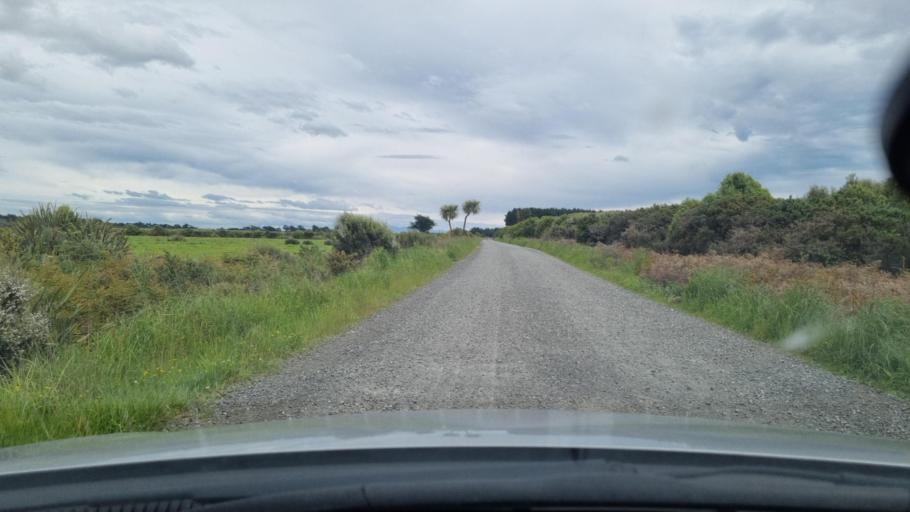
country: NZ
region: Southland
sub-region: Invercargill City
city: Invercargill
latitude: -46.4043
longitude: 168.2792
